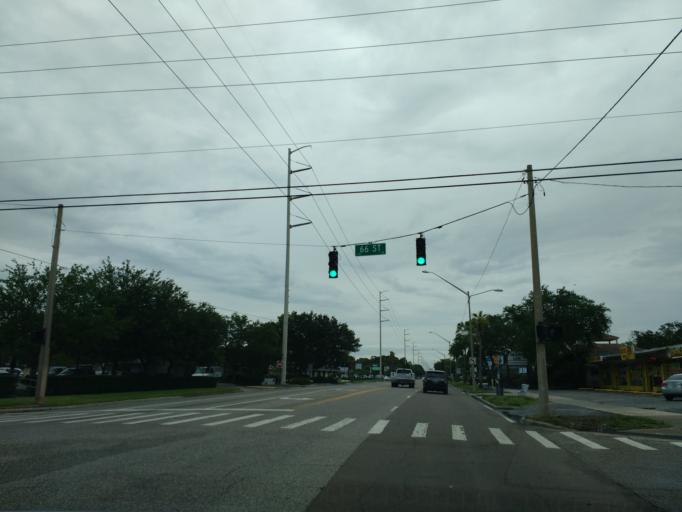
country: US
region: Florida
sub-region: Pinellas County
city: South Pasadena
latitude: 27.7708
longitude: -82.7284
